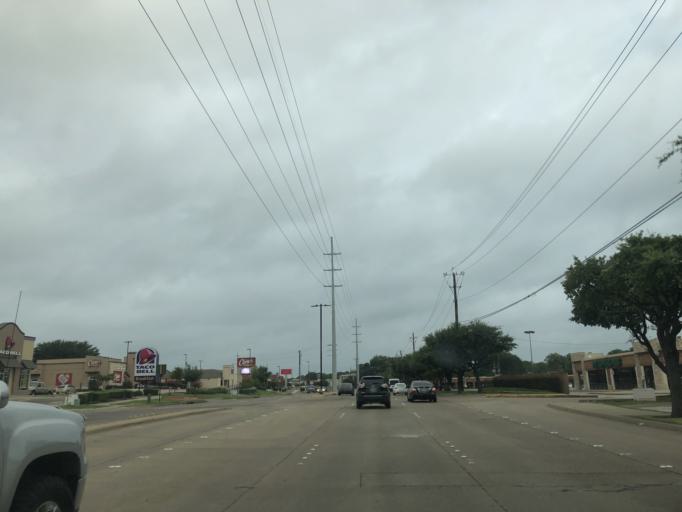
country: US
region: Texas
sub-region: Dallas County
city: Garland
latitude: 32.8620
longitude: -96.6433
